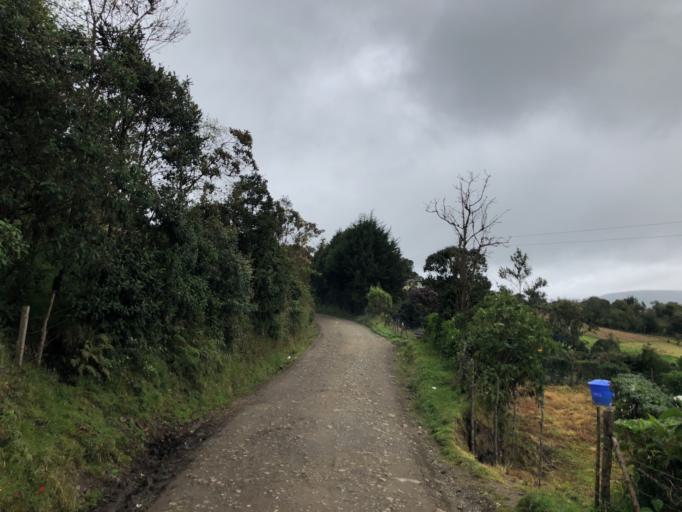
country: CO
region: Cauca
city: Totoro
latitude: 2.4967
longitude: -76.3465
